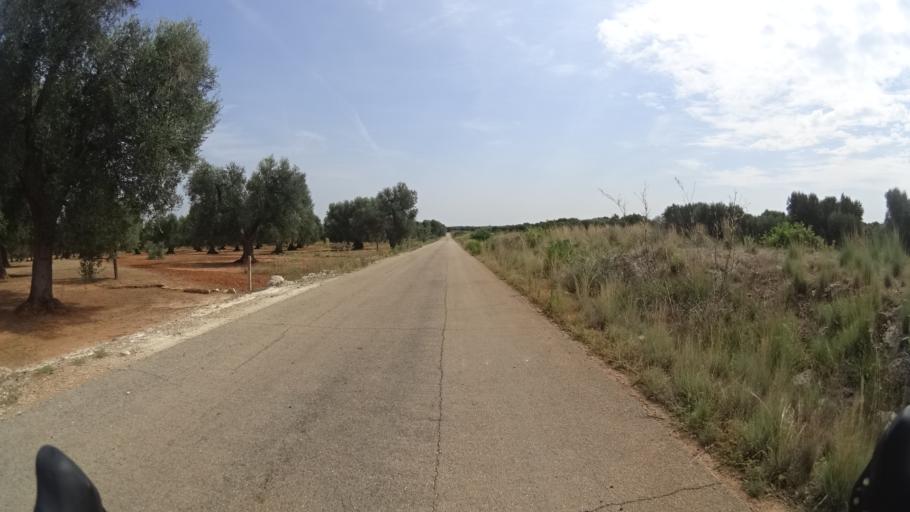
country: IT
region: Apulia
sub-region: Provincia di Lecce
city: Porto Cesareo
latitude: 40.3234
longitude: 17.8944
